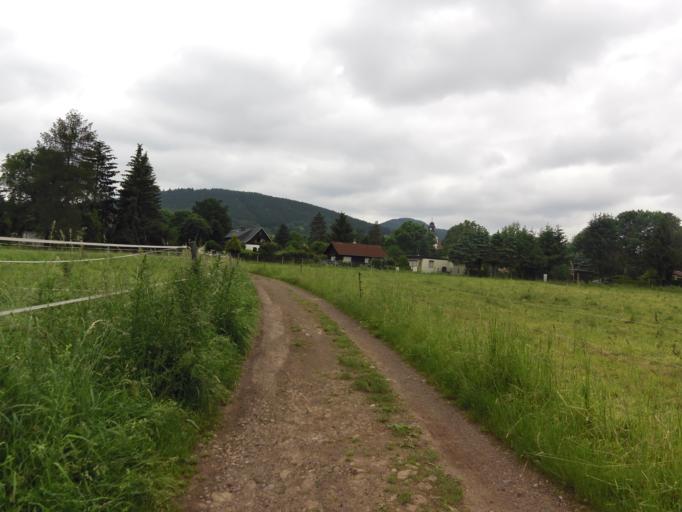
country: DE
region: Thuringia
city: Tabarz
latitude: 50.8800
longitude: 10.5164
